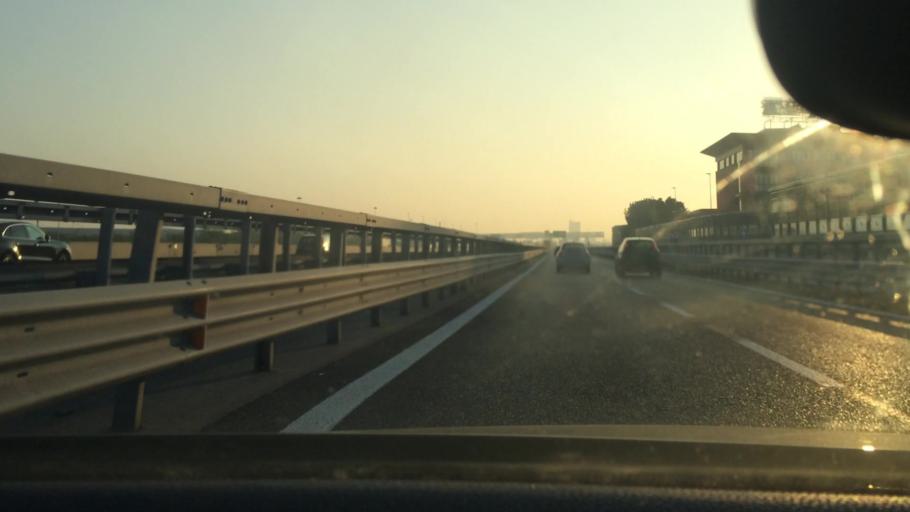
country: IT
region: Lombardy
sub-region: Citta metropolitana di Milano
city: Pero
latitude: 45.5138
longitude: 9.0899
